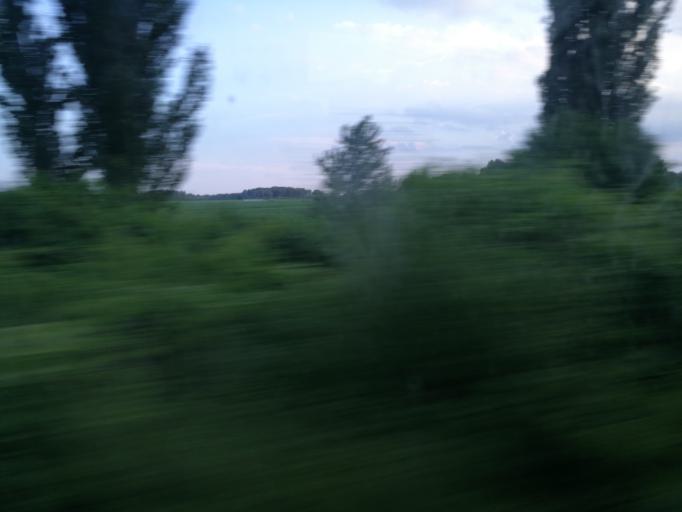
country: RO
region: Dambovita
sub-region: Comuna Contesti
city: Contesti
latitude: 44.6567
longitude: 25.6530
